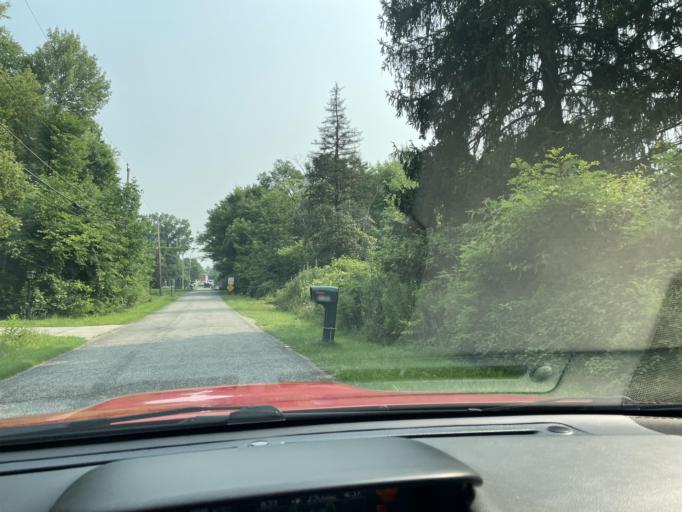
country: US
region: Ohio
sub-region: Trumbull County
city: McDonald
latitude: 41.1589
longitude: -80.7365
